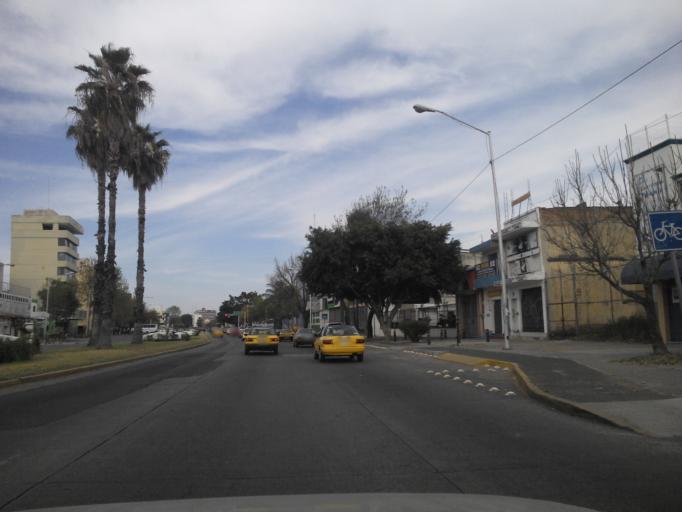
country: MX
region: Jalisco
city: Guadalajara
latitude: 20.6638
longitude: -103.3563
